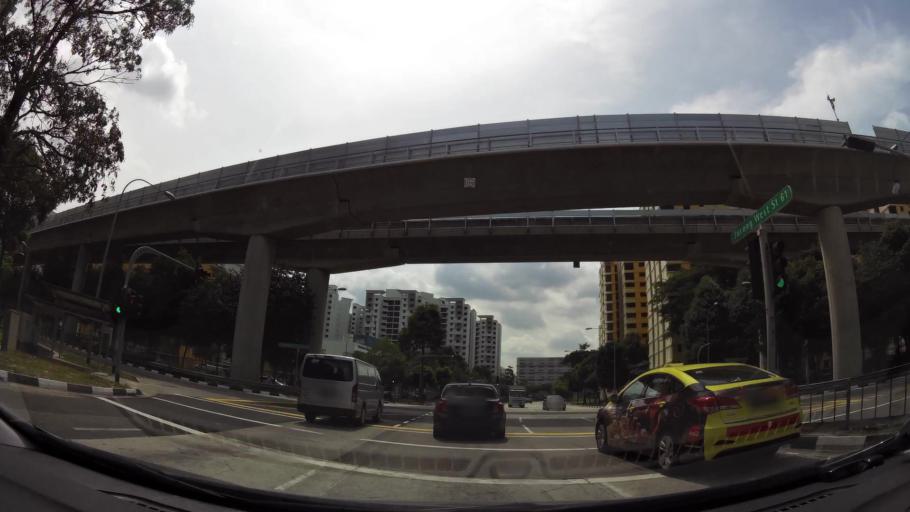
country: MY
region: Johor
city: Johor Bahru
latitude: 1.3378
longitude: 103.6988
